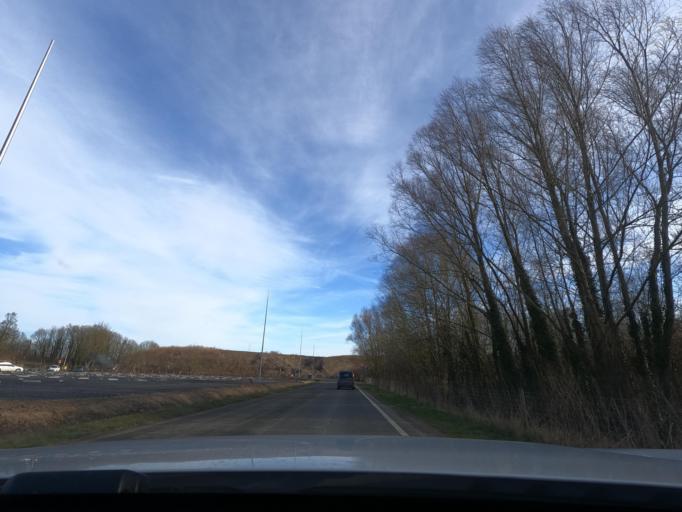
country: BE
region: Wallonia
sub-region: Province du Hainaut
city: Lens
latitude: 50.5837
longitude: 3.8949
